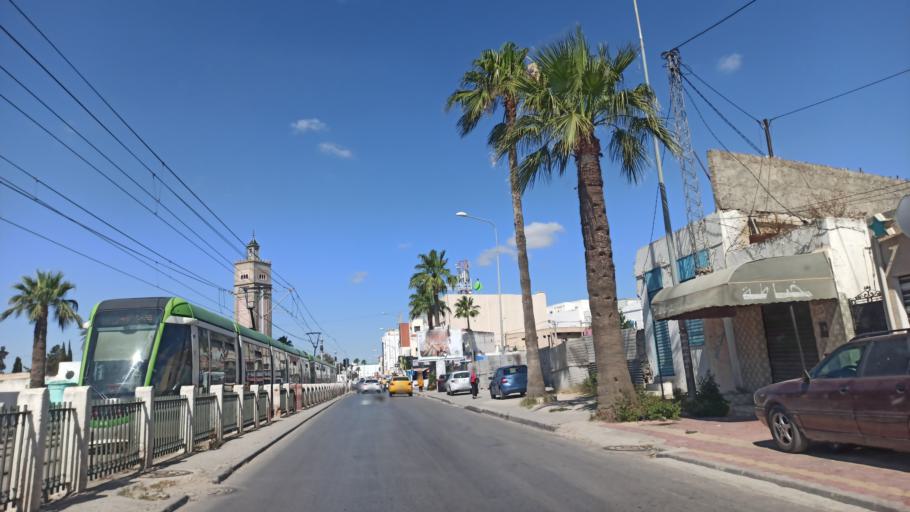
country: TN
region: Manouba
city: Manouba
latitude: 36.8028
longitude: 10.1147
